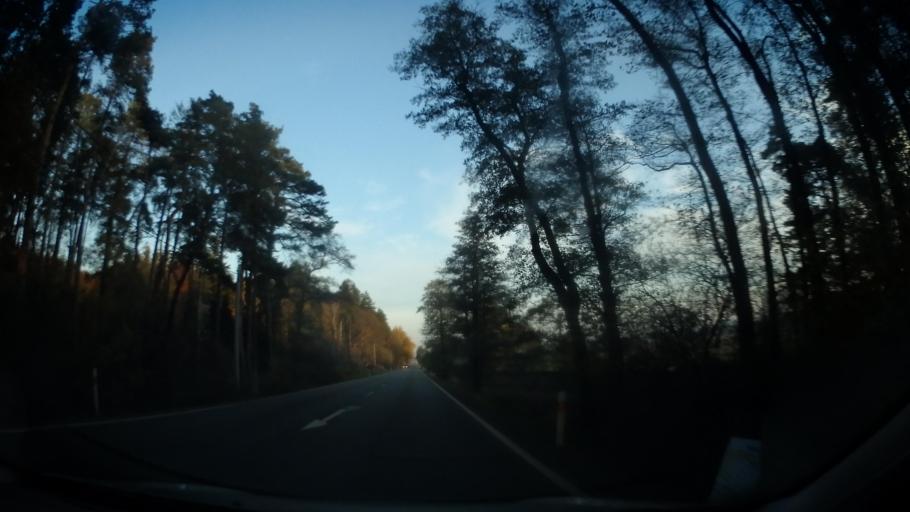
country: CZ
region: Central Bohemia
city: Vlasim
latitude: 49.7152
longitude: 14.8418
